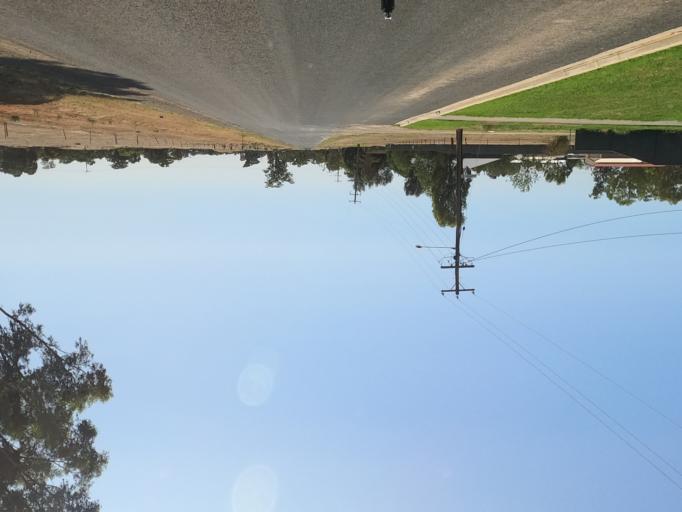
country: AU
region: New South Wales
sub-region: Corowa Shire
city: Mulwala
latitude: -35.9825
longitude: 146.0016
